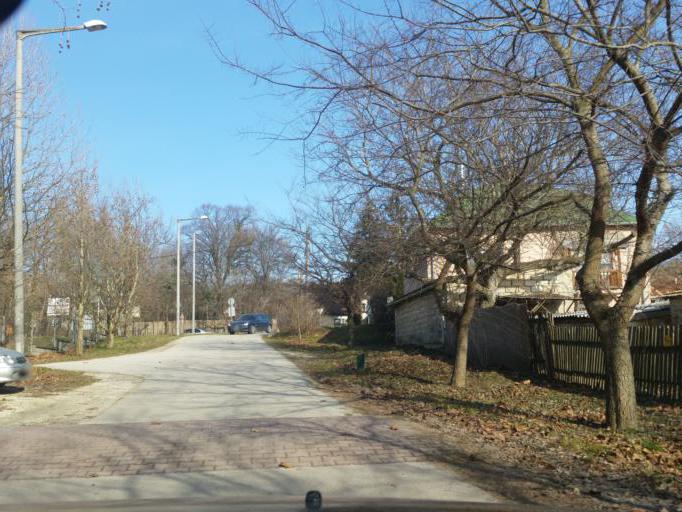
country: HU
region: Pest
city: Telki
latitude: 47.5581
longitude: 18.7992
